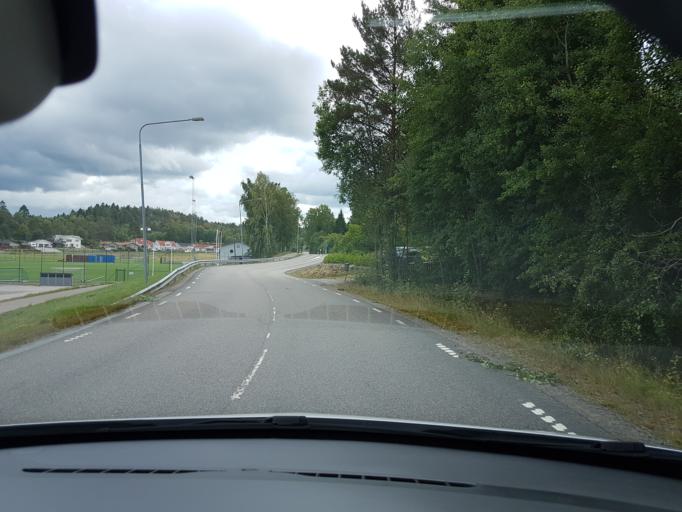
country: SE
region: Vaestra Goetaland
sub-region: Ale Kommun
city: Nodinge-Nol
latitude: 57.8871
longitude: 12.0760
